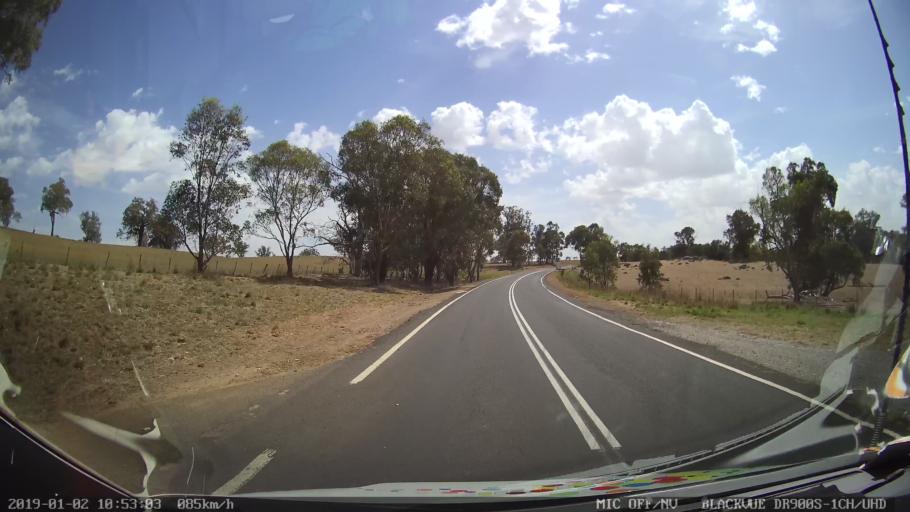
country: AU
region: New South Wales
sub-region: Cootamundra
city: Cootamundra
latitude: -34.6817
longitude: 148.2718
